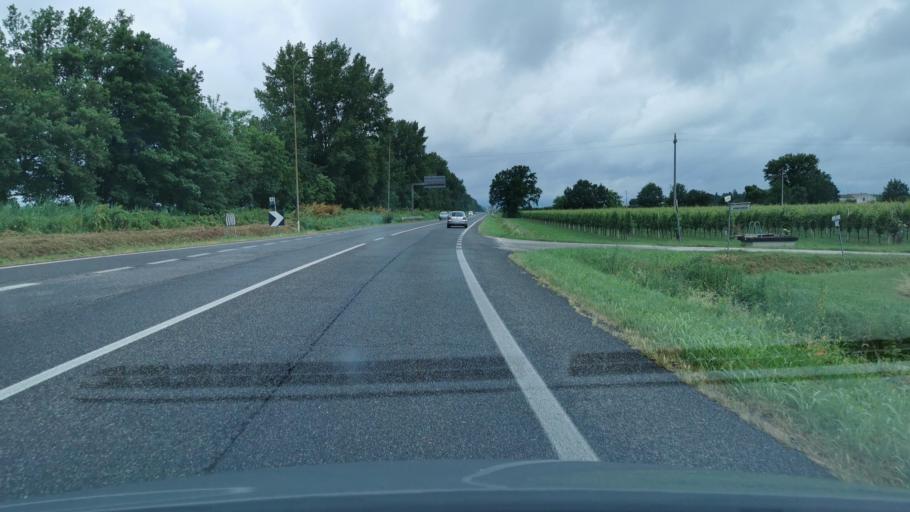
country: IT
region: Emilia-Romagna
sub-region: Provincia di Ravenna
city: Granarolo
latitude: 44.3497
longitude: 11.9267
